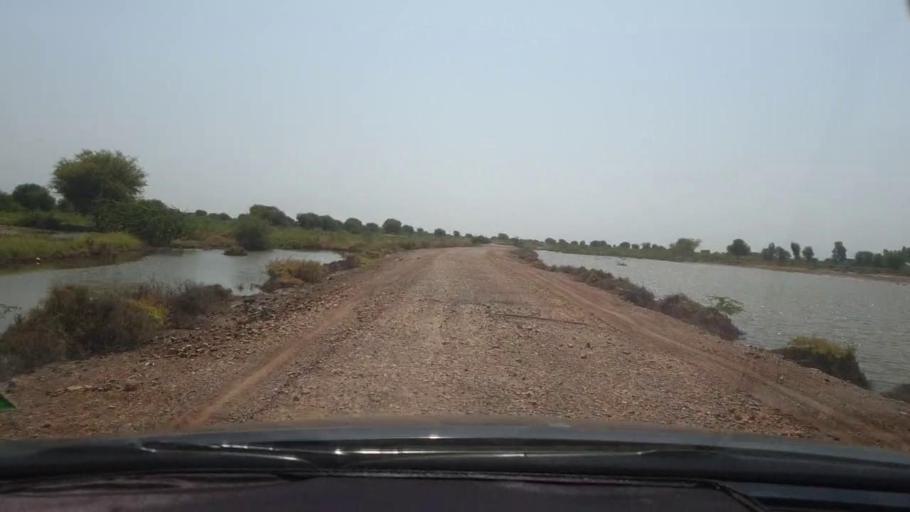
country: PK
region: Sindh
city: Tando Bago
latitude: 24.8090
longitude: 69.1661
